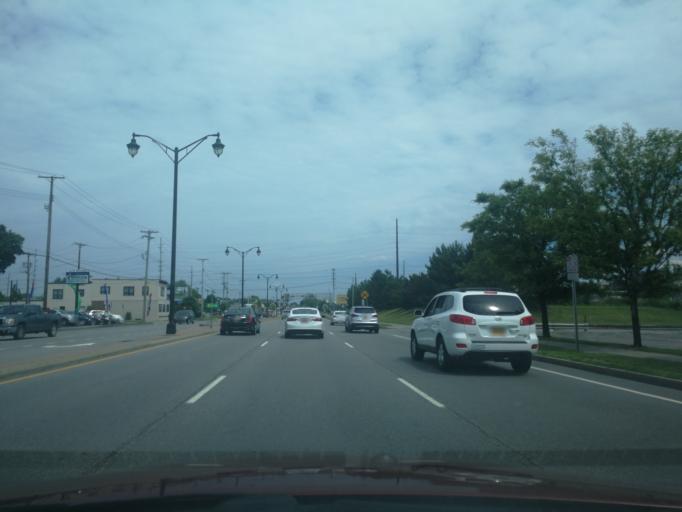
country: US
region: New York
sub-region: Monroe County
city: Greece
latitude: 43.2031
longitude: -77.6506
